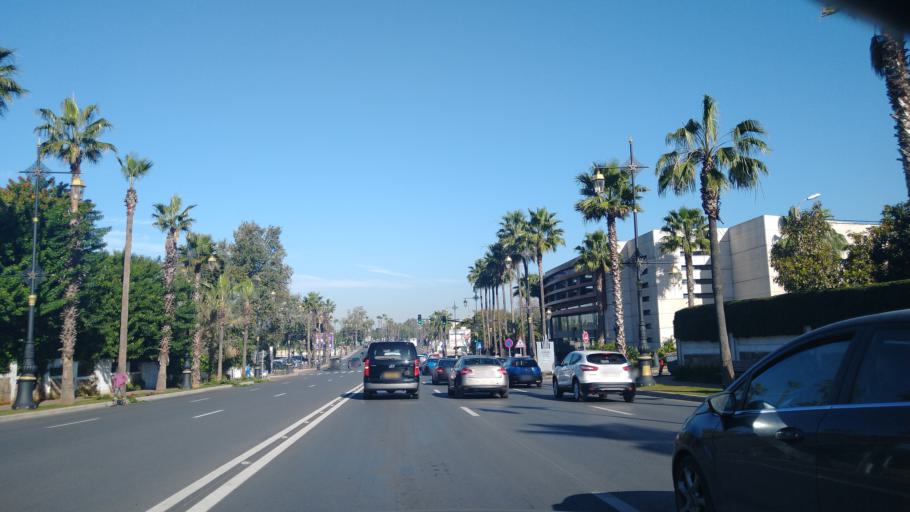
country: MA
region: Rabat-Sale-Zemmour-Zaer
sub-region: Rabat
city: Rabat
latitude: 33.9985
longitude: -6.8274
